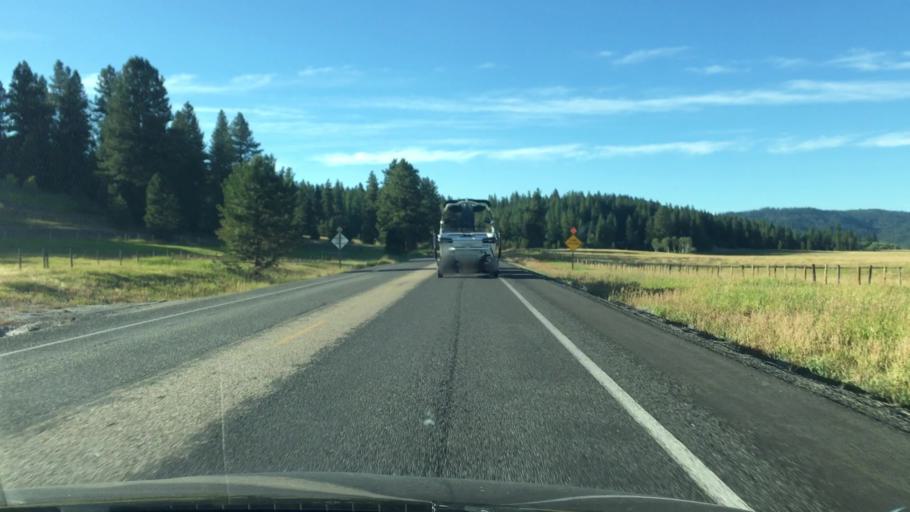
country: US
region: Idaho
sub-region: Valley County
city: Cascade
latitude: 44.5548
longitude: -116.0281
